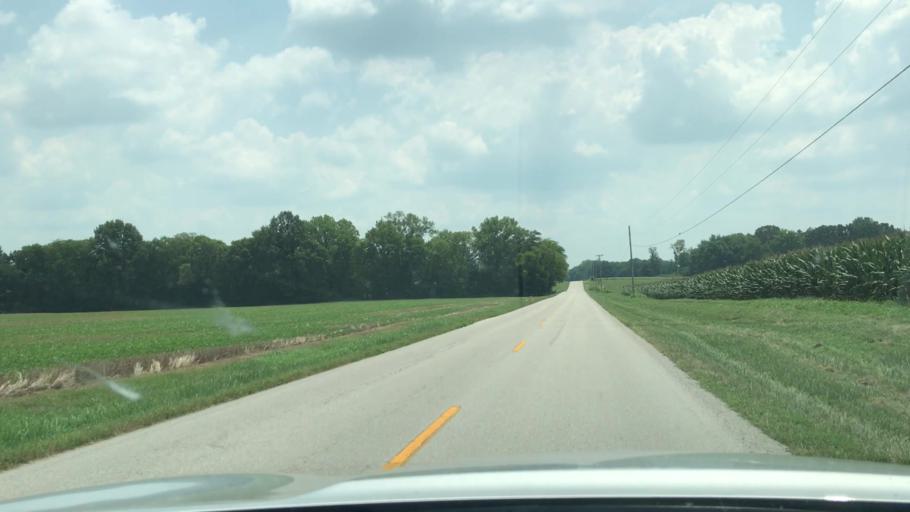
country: US
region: Kentucky
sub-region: Todd County
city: Elkton
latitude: 36.7665
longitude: -87.1107
